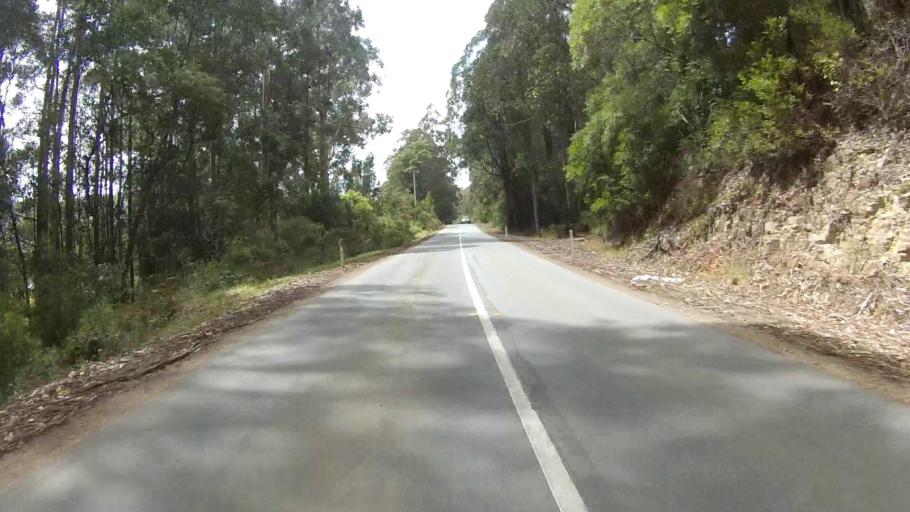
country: AU
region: Tasmania
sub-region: Kingborough
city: Kettering
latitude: -43.1297
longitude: 147.1598
